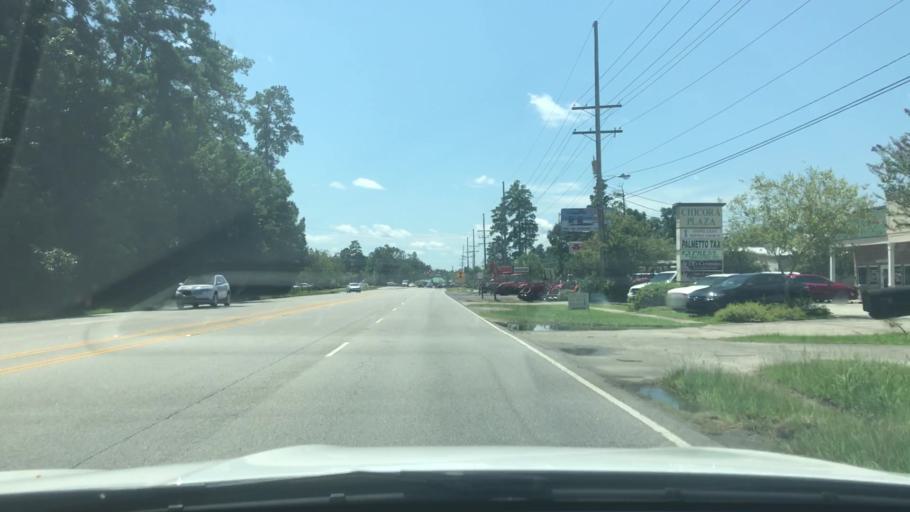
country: US
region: South Carolina
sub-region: Horry County
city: Conway
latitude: 33.8700
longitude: -79.0523
